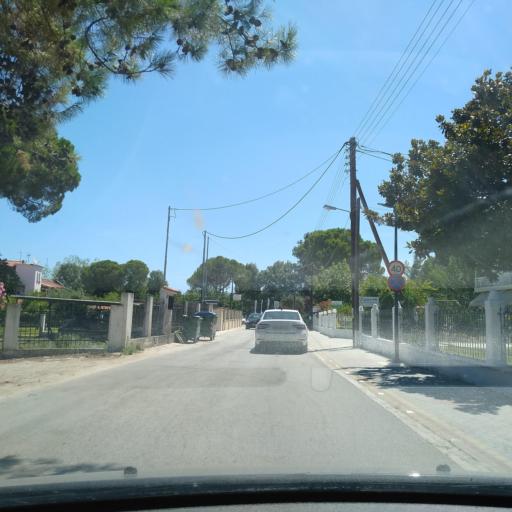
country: GR
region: Central Macedonia
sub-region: Nomos Chalkidikis
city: Neos Marmaras
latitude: 40.1878
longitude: 23.7964
